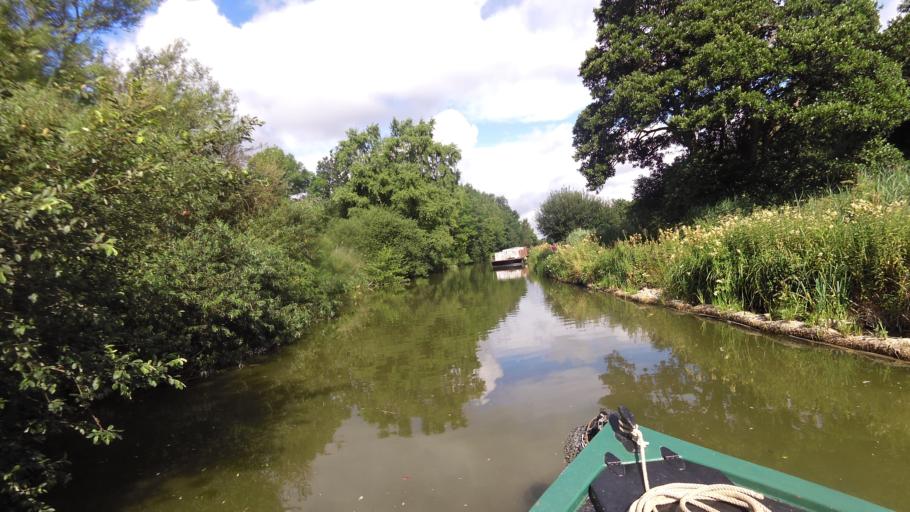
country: GB
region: England
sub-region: West Berkshire
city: Kintbury
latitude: 51.4028
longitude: -1.4599
